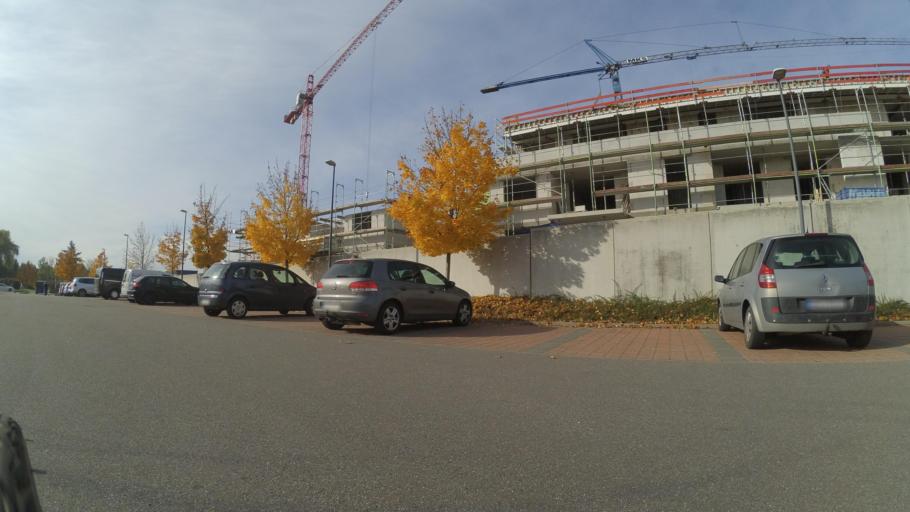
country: DE
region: Baden-Wuerttemberg
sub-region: Regierungsbezirk Stuttgart
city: Ohringen
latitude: 49.2004
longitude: 9.5178
